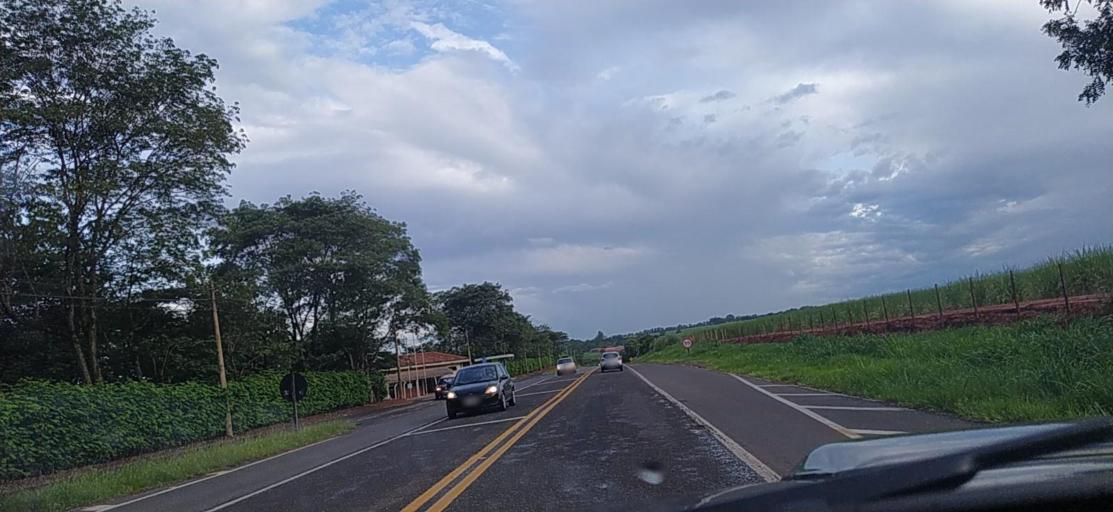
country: BR
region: Sao Paulo
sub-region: Catanduva
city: Catanduva
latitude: -21.1552
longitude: -48.9537
